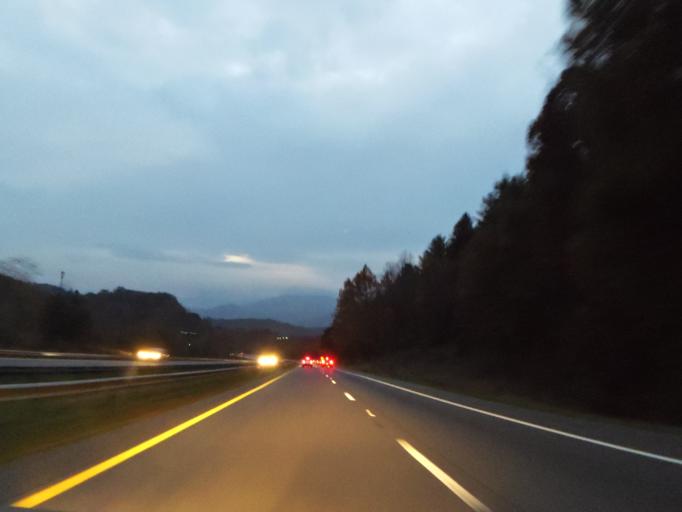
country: US
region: North Carolina
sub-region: McDowell County
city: West Marion
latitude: 35.6382
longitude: -82.1094
